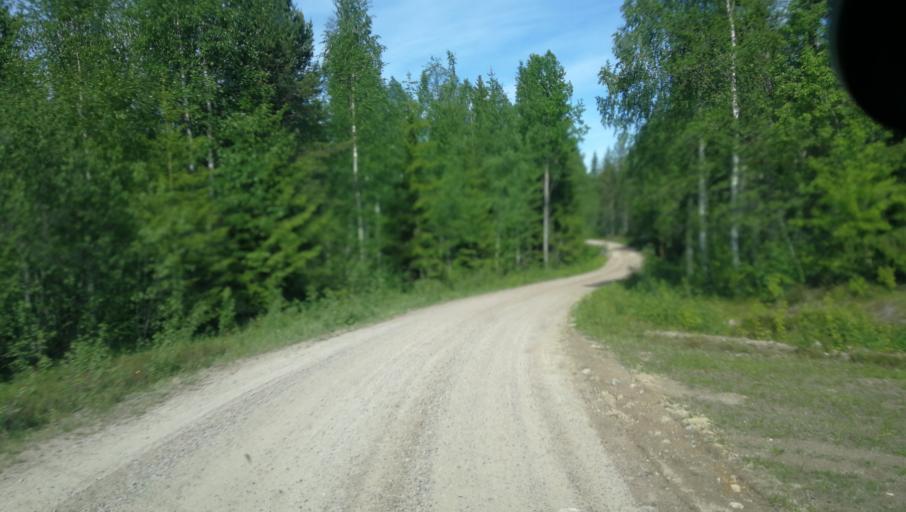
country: SE
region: Dalarna
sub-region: Vansbro Kommun
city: Vansbro
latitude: 60.8338
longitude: 14.1568
